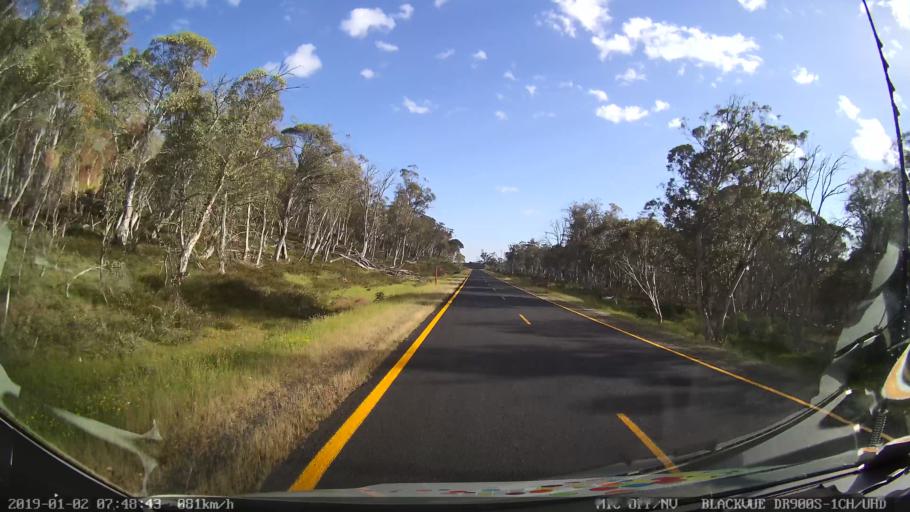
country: AU
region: New South Wales
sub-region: Tumut Shire
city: Tumut
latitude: -35.7499
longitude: 148.5194
